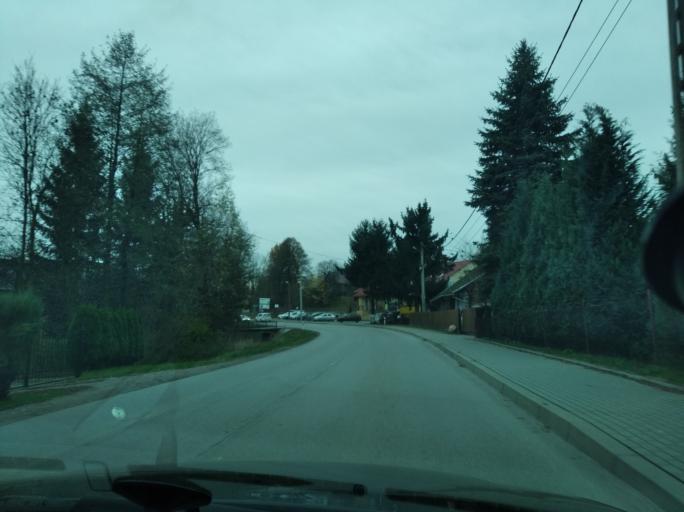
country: PL
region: Subcarpathian Voivodeship
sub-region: Powiat lancucki
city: Krzemienica
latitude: 50.0753
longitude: 22.1887
